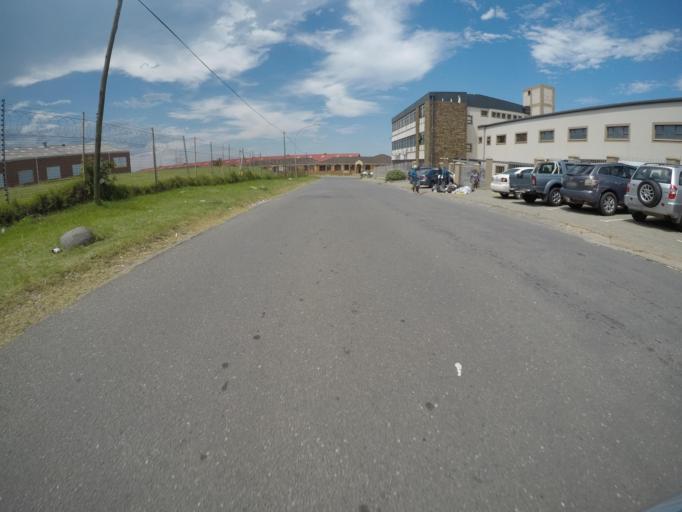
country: ZA
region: Eastern Cape
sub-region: Buffalo City Metropolitan Municipality
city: East London
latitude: -33.0322
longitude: 27.8788
